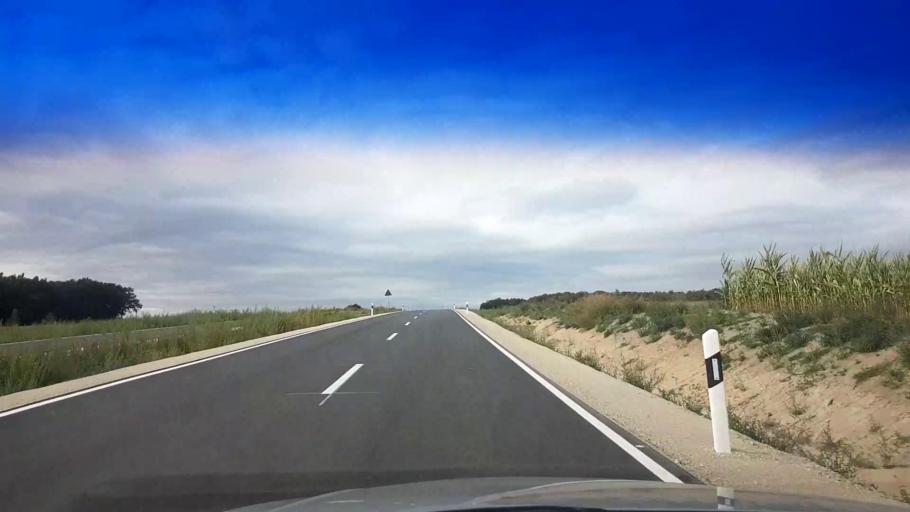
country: DE
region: Bavaria
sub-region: Upper Franconia
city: Frensdorf
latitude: 49.7993
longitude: 10.8770
